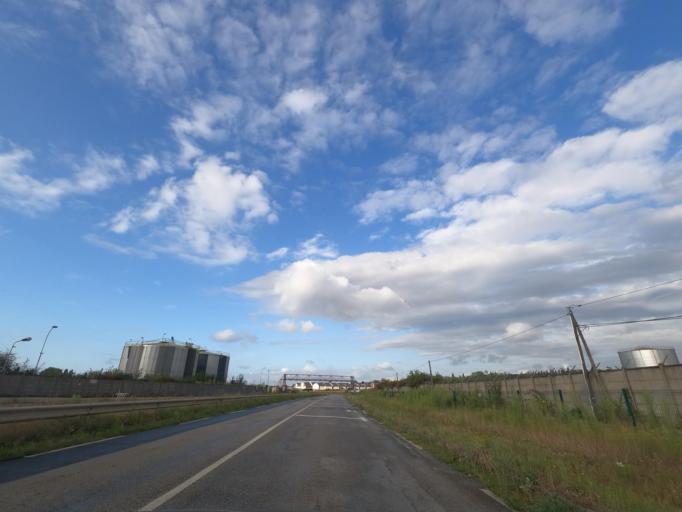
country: FR
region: Haute-Normandie
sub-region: Departement de la Seine-Maritime
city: Petit-Couronne
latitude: 49.3786
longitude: 1.0123
